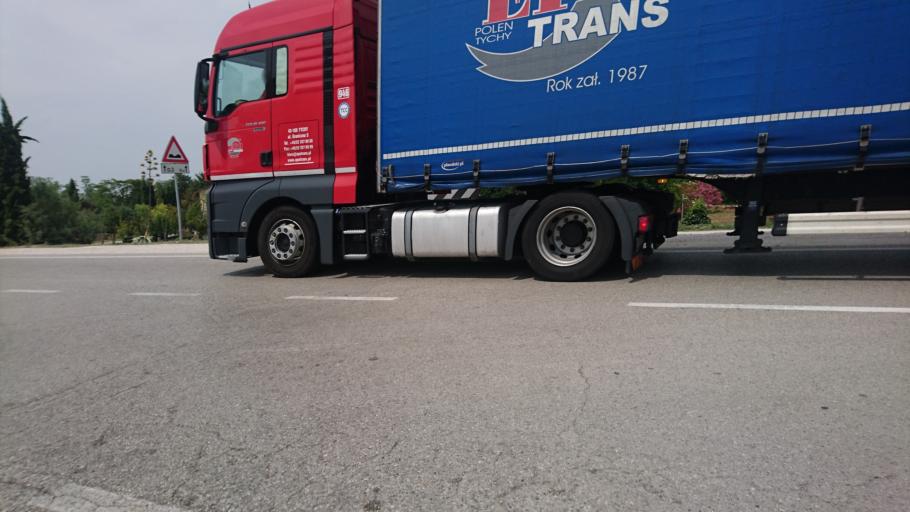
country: IT
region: Veneto
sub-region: Provincia di Rovigo
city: Rosolina
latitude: 45.0680
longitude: 12.2422
